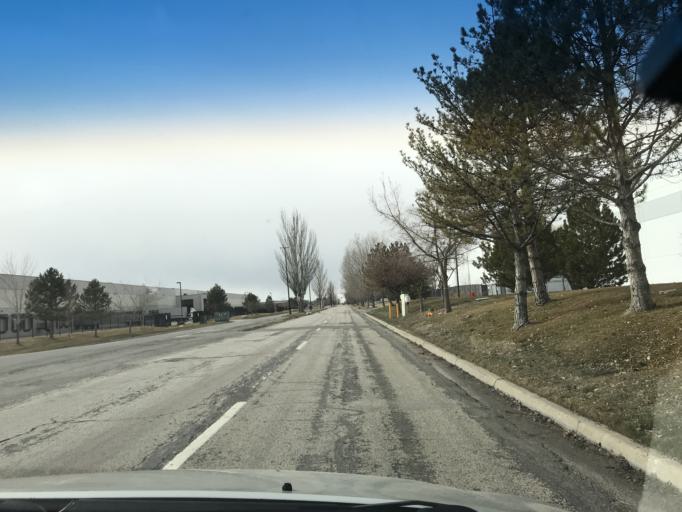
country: US
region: Utah
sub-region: Salt Lake County
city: West Valley City
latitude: 40.7814
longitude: -112.0195
